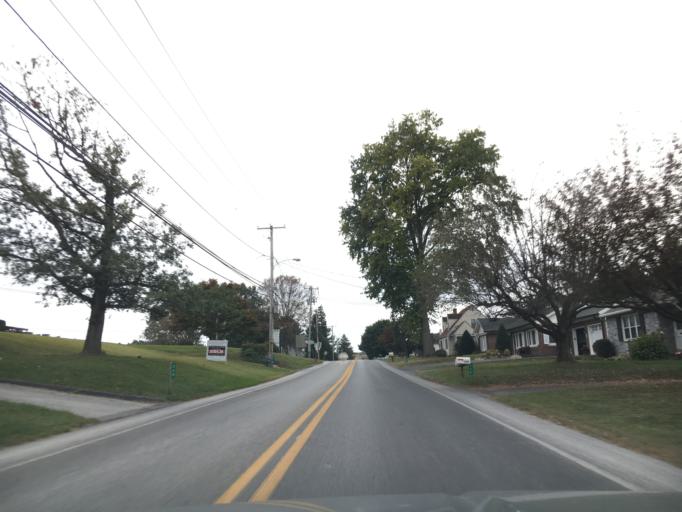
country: US
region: Pennsylvania
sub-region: Lancaster County
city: Quarryville
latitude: 39.8938
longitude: -76.1741
